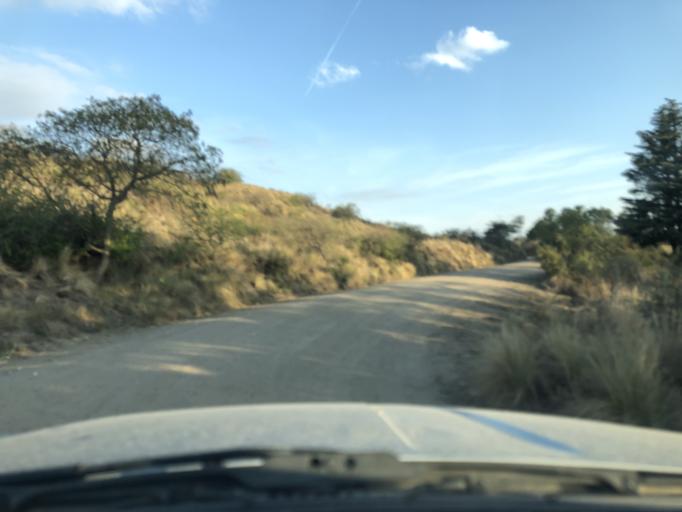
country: AR
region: Cordoba
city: Agua de Oro
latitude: -31.0602
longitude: -64.3484
